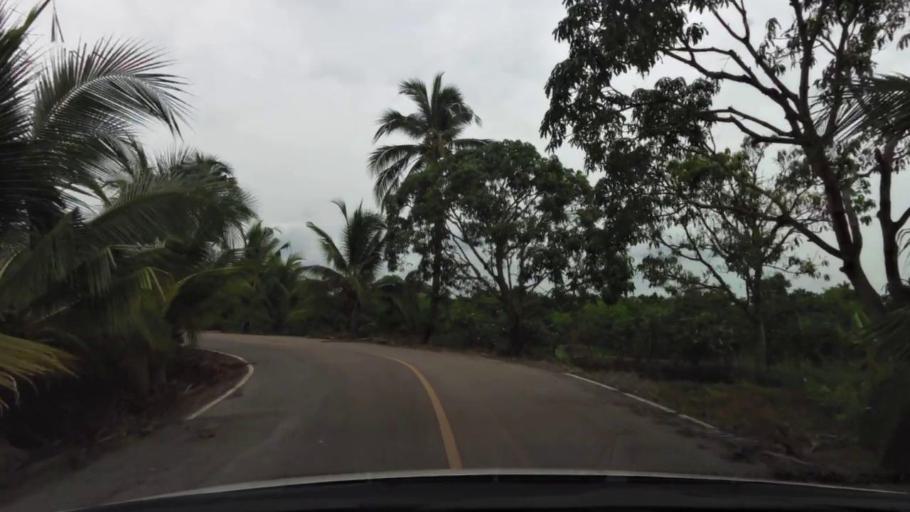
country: TH
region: Samut Sakhon
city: Ban Phaeo
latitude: 13.5882
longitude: 100.0353
